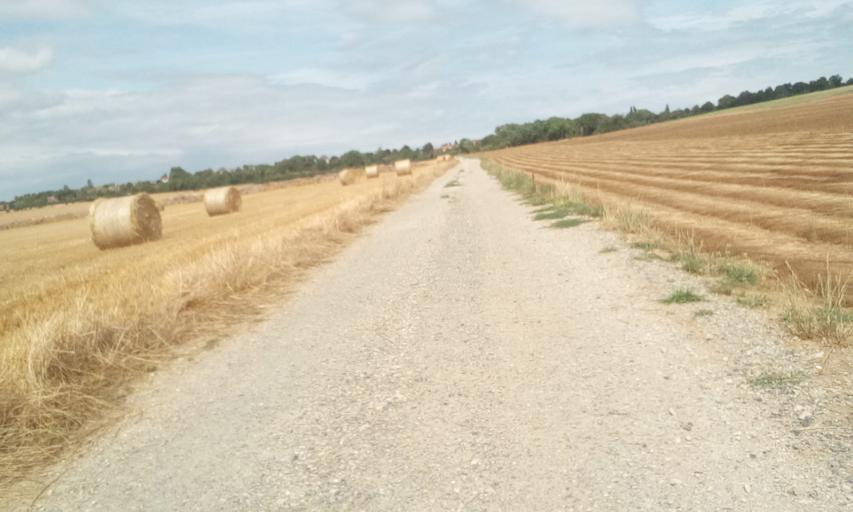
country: FR
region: Lower Normandy
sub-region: Departement du Calvados
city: Herouvillette
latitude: 49.2311
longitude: -0.2339
